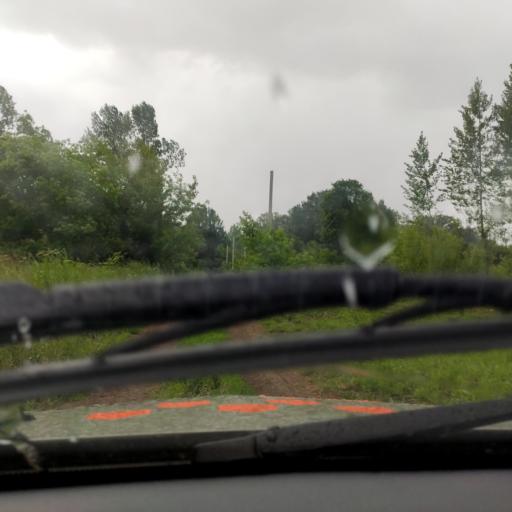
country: RU
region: Bashkortostan
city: Ufa
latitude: 54.7829
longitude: 56.1908
